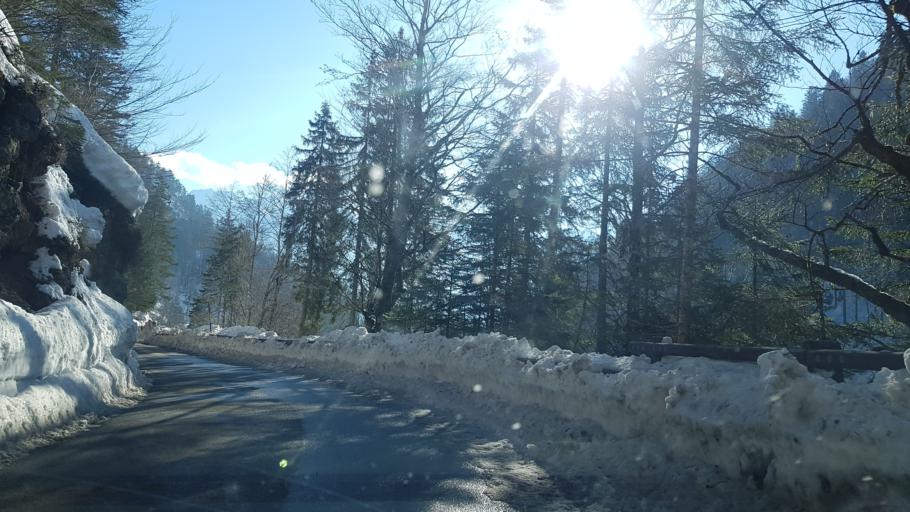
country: IT
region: Friuli Venezia Giulia
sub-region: Provincia di Udine
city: Malborghetto
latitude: 46.5246
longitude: 13.4737
